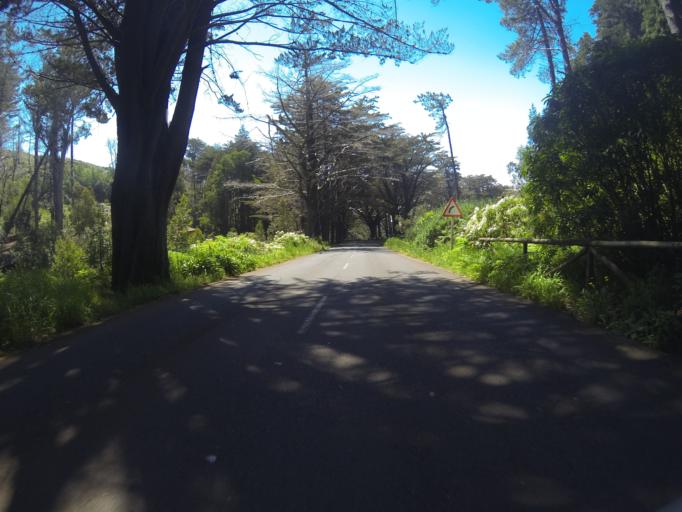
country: PT
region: Madeira
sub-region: Funchal
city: Nossa Senhora do Monte
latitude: 32.6961
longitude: -16.9034
